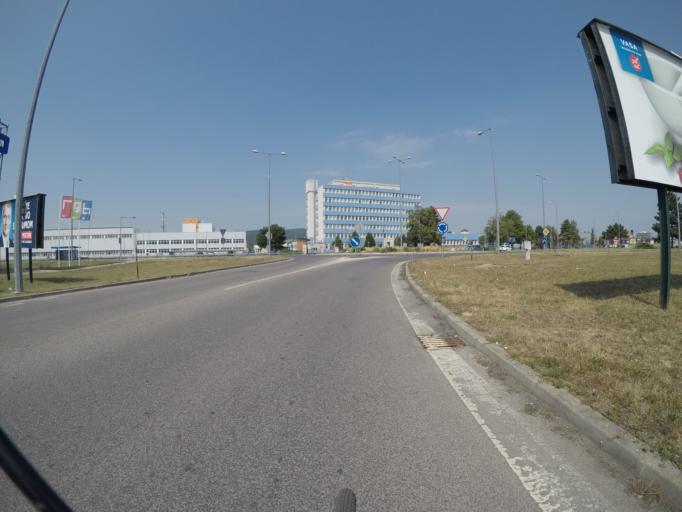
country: SK
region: Trenciansky
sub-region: Okres Nove Mesto nad Vahom
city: Nove Mesto nad Vahom
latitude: 48.7431
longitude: 17.8380
